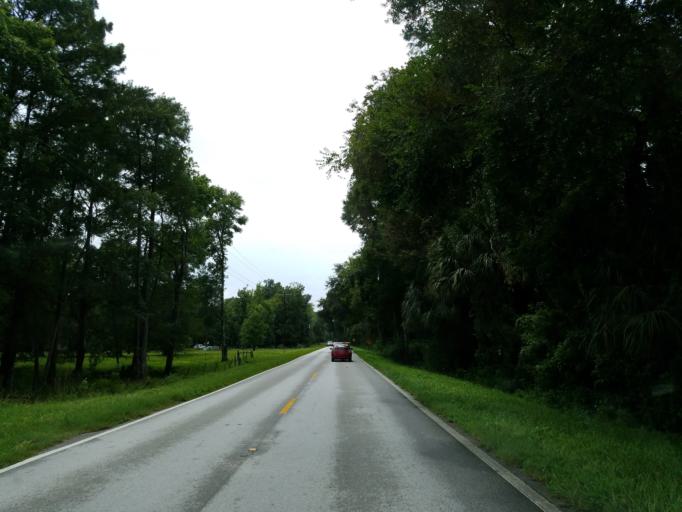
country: US
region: Florida
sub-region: Sumter County
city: Bushnell
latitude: 28.6910
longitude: -82.2034
